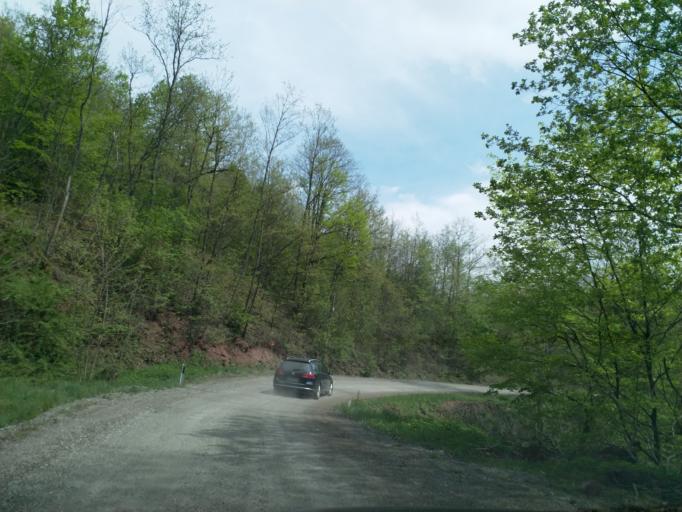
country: RS
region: Central Serbia
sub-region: Pomoravski Okrug
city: Despotovac
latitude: 43.9579
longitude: 21.5666
